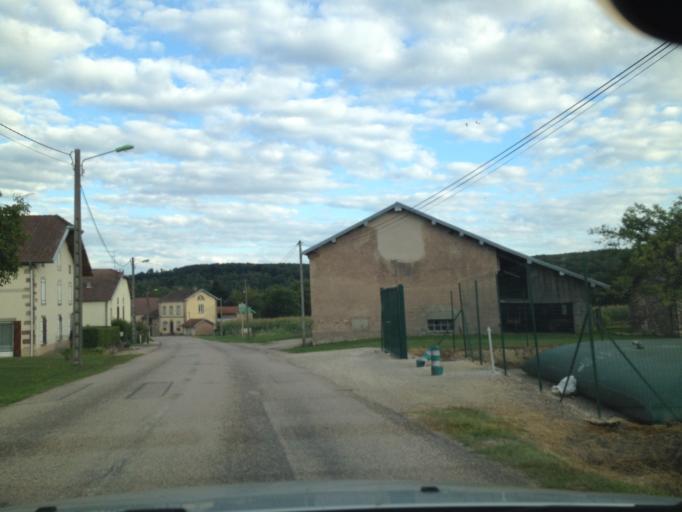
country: FR
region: Lorraine
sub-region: Departement des Vosges
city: Bains-les-Bains
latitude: 47.9742
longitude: 6.1734
